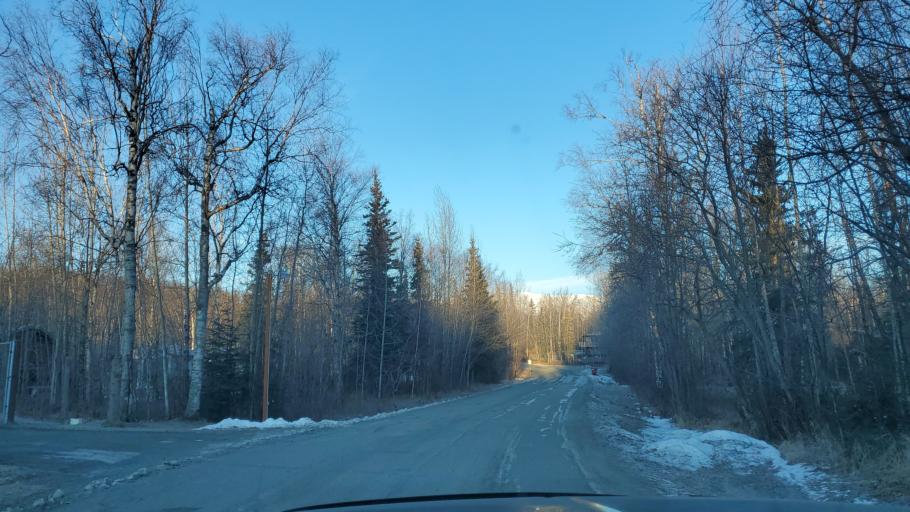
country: US
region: Alaska
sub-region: Matanuska-Susitna Borough
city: Tanaina
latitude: 61.6077
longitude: -149.4037
